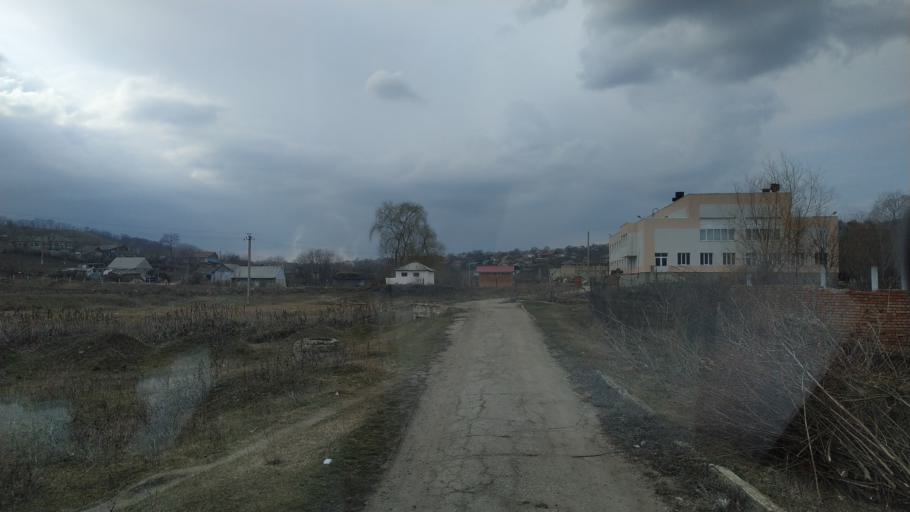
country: MD
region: Anenii Noi
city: Varnita
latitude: 46.8395
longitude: 29.3599
